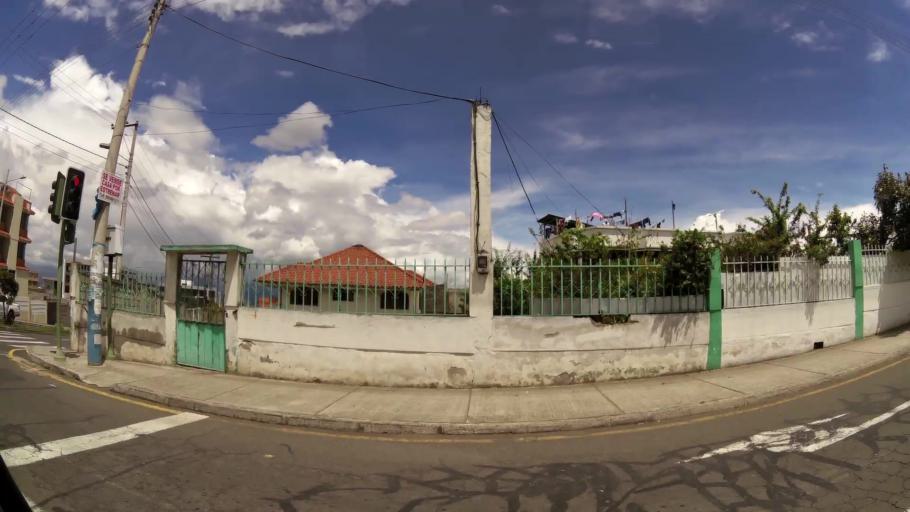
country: EC
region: Tungurahua
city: Ambato
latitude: -1.2759
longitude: -78.6397
